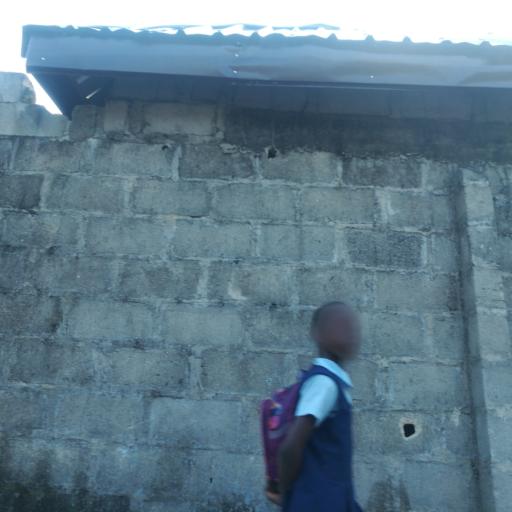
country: NG
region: Rivers
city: Port Harcourt
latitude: 4.8492
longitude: 6.9603
